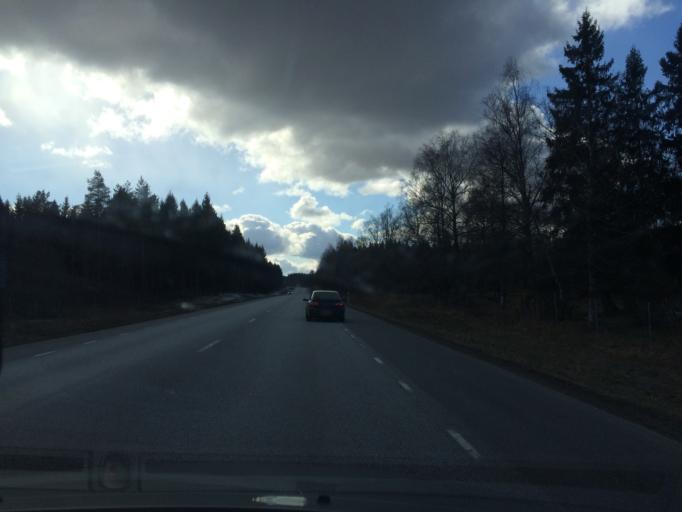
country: SE
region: Vaestra Goetaland
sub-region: Mariestads Kommun
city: Mariestad
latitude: 58.6282
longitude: 13.6754
